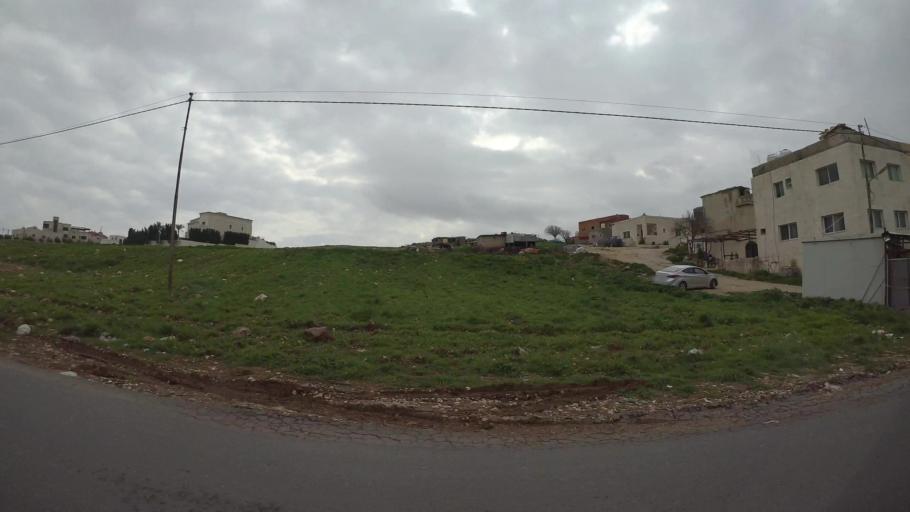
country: JO
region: Amman
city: Wadi as Sir
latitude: 31.9301
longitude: 35.8532
